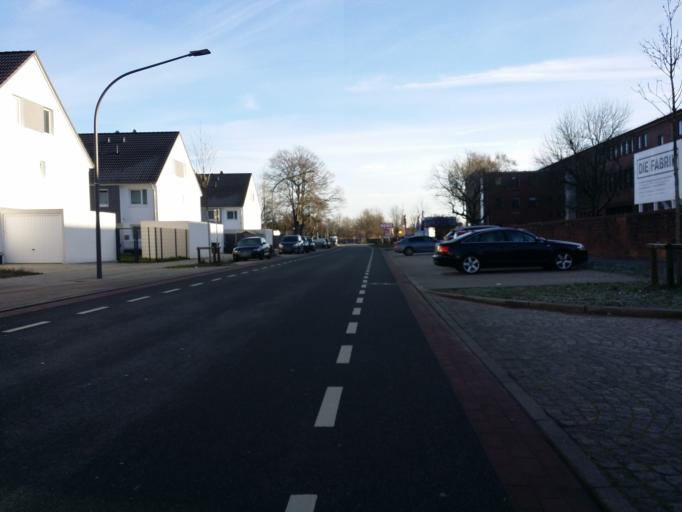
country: DE
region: Bremen
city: Bremen
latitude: 53.0781
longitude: 8.7718
